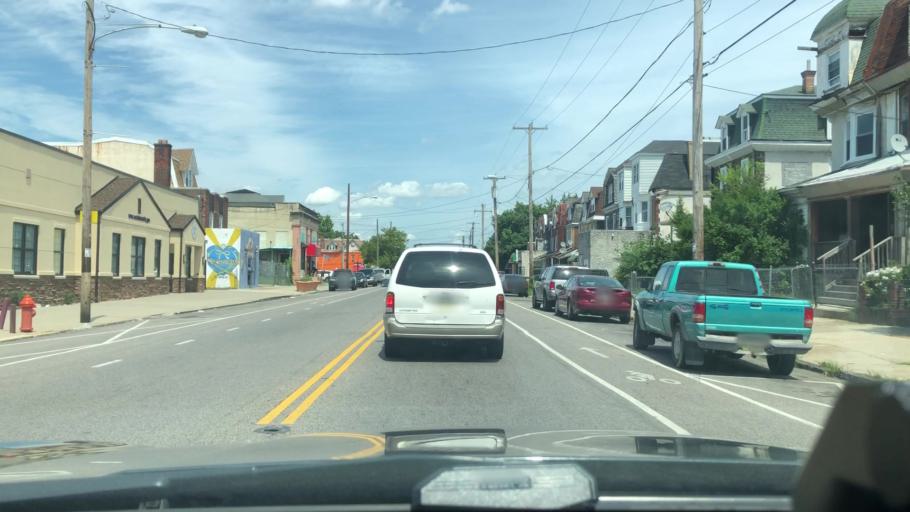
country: US
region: Pennsylvania
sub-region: Montgomery County
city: Wyndmoor
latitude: 40.0442
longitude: -75.1661
